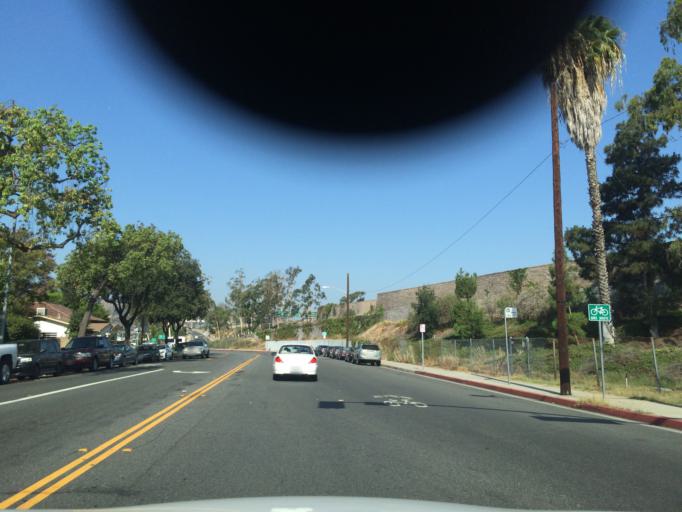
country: US
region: California
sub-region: Los Angeles County
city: North Glendale
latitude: 34.1541
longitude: -118.2712
